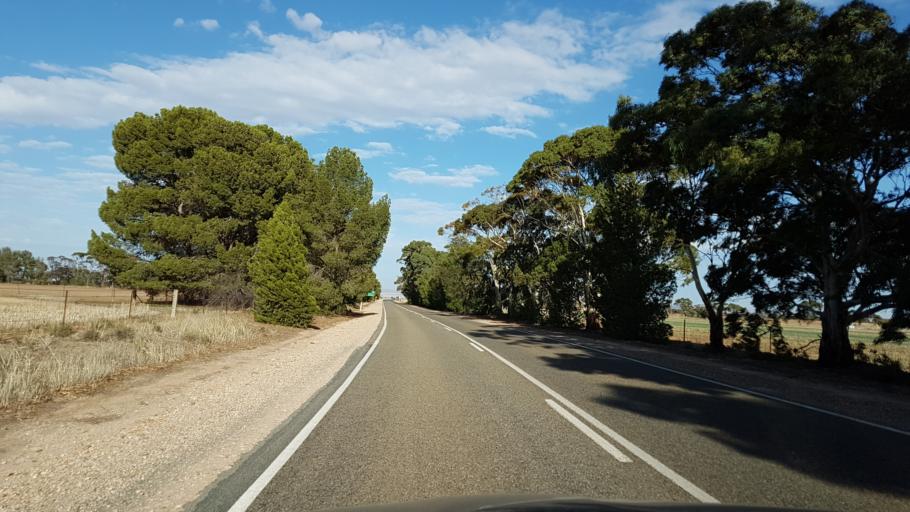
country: AU
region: South Australia
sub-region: Clare and Gilbert Valleys
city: Clare
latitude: -33.6941
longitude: 138.4229
